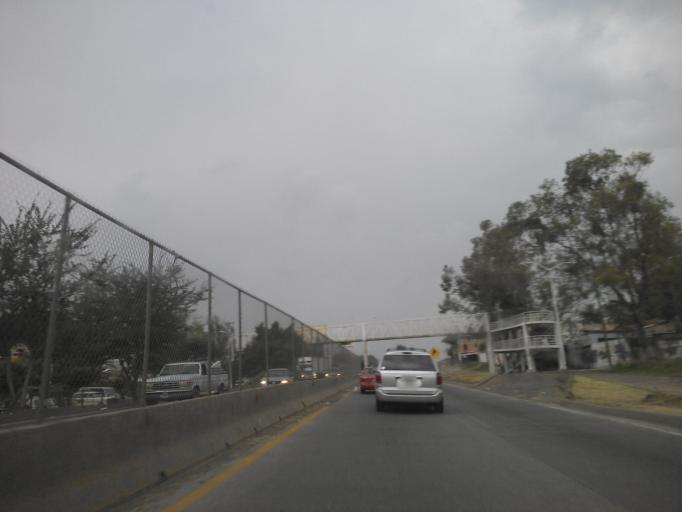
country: MX
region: Jalisco
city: Tlaquepaque
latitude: 20.6103
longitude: -103.2778
